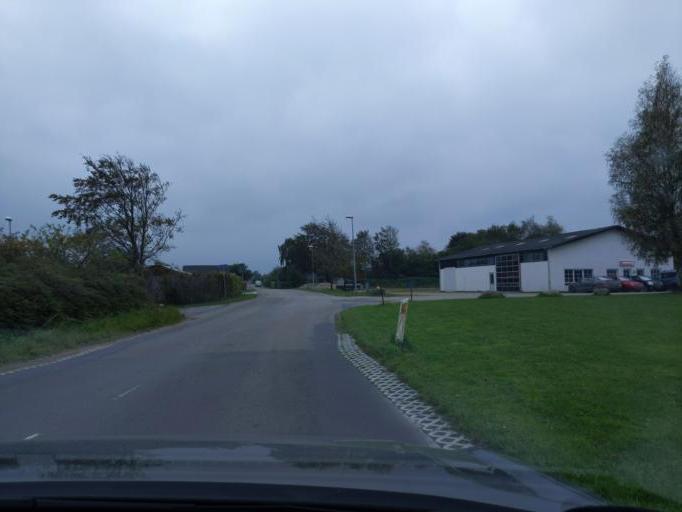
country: DK
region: Central Jutland
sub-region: Viborg Kommune
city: Viborg
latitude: 56.3642
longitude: 9.2960
